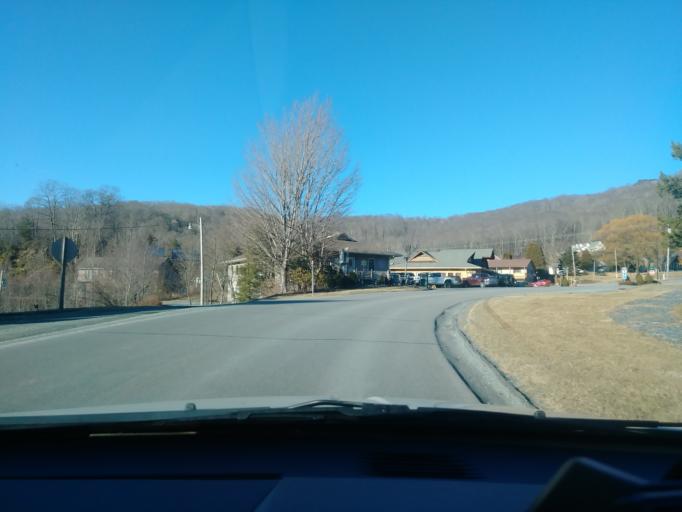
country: US
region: North Carolina
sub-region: Avery County
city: Banner Elk
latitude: 36.1350
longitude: -81.8463
